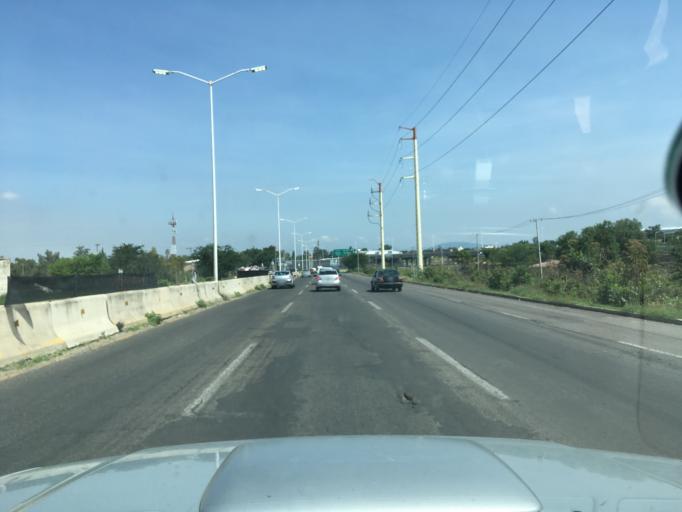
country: MX
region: Jalisco
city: Tonala
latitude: 20.6812
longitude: -103.2433
